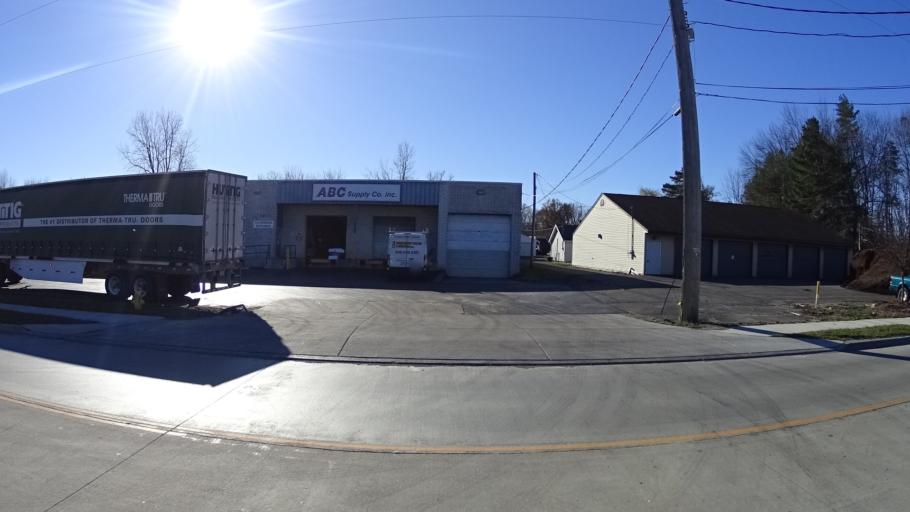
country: US
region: Ohio
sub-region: Lorain County
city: Sheffield
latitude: 41.4004
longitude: -82.1256
